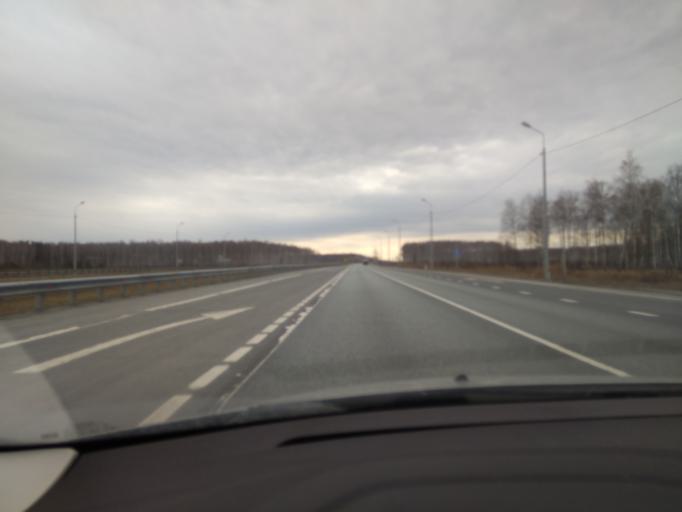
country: RU
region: Chelyabinsk
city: Chebarkul'
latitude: 54.9104
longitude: 60.4330
